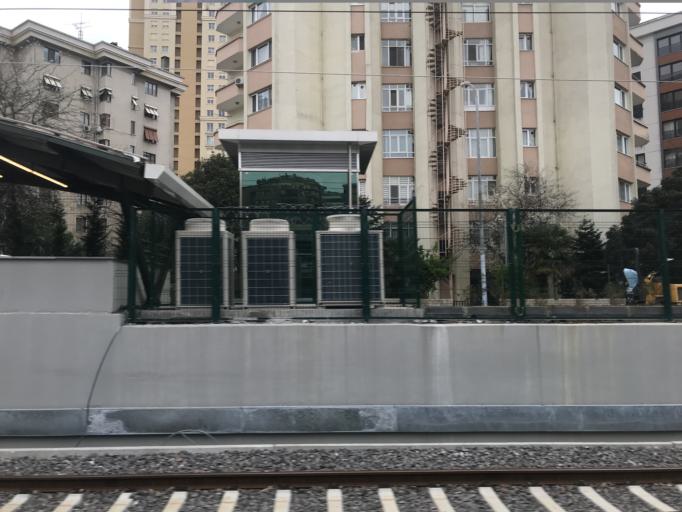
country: TR
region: Istanbul
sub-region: Atasehir
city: Atasehir
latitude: 40.9716
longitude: 29.0762
